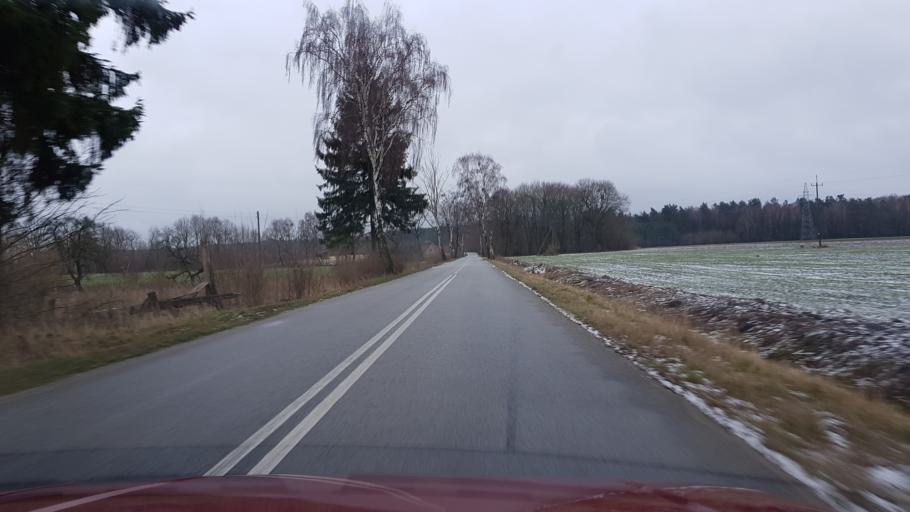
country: PL
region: West Pomeranian Voivodeship
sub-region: Powiat lobeski
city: Resko
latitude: 53.8223
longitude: 15.3954
